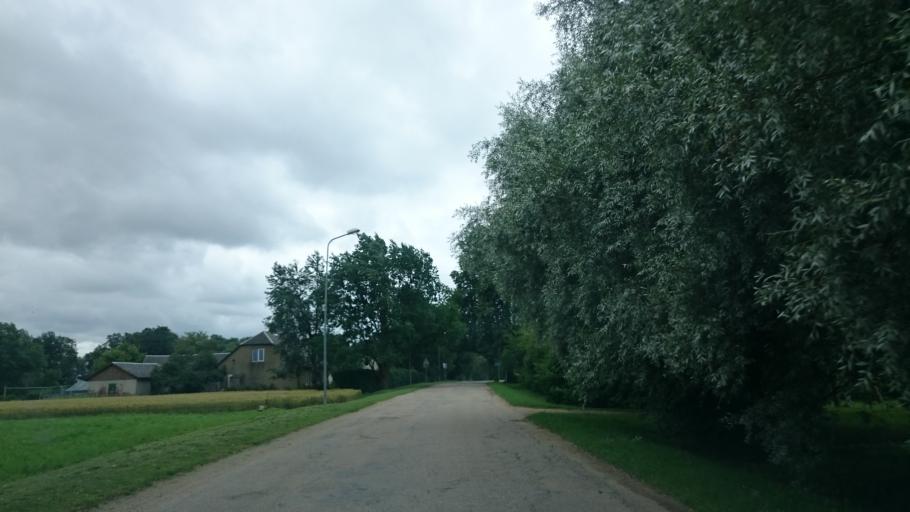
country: LV
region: Durbe
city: Liegi
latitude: 56.7394
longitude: 21.3811
